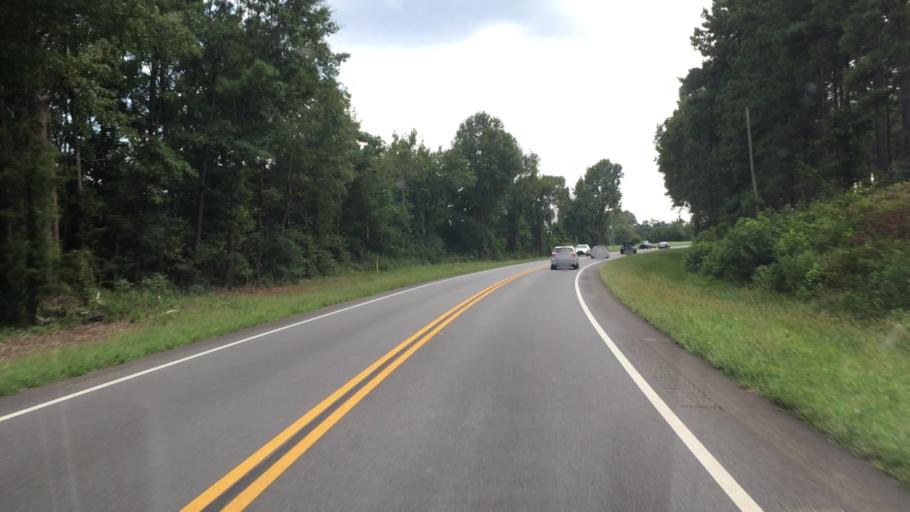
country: US
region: Georgia
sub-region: Putnam County
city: Eatonton
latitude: 33.3950
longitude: -83.3688
